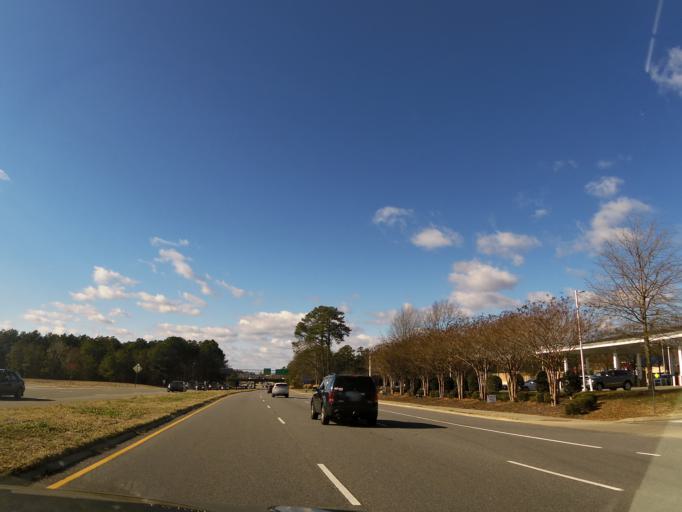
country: US
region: Virginia
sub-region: Henrico County
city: Short Pump
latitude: 37.6479
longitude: -77.5890
